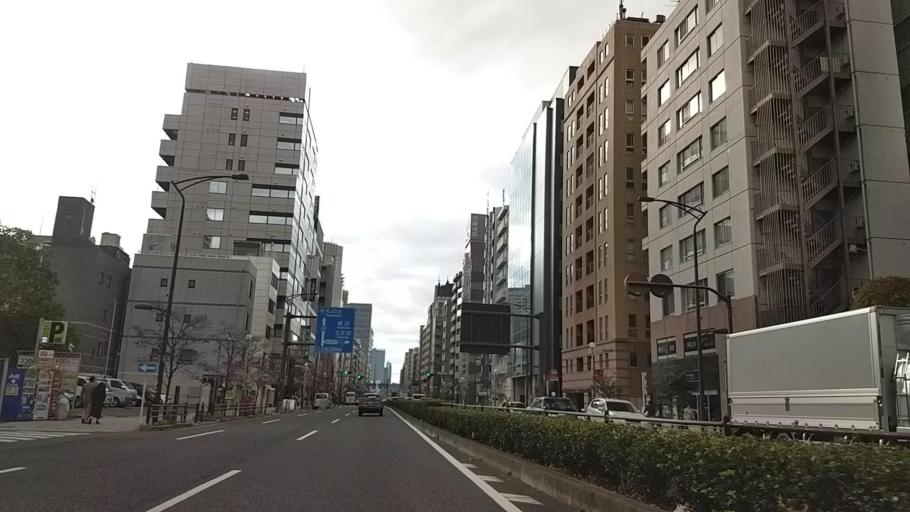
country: JP
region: Tokyo
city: Tokyo
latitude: 35.6515
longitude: 139.7450
